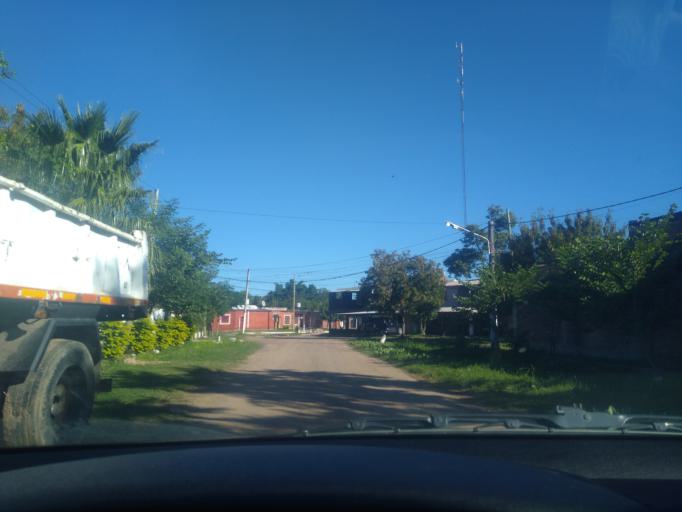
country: AR
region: Chaco
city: Puerto Vilelas
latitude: -27.5165
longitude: -58.9433
